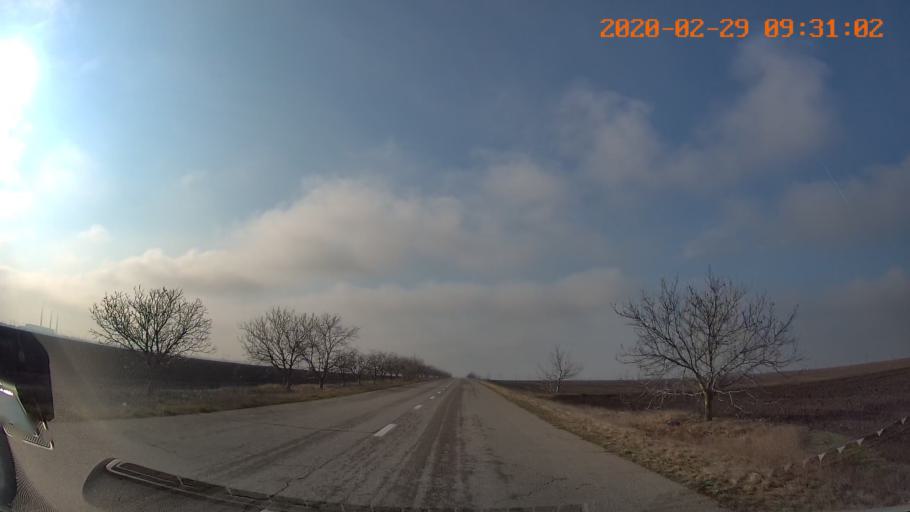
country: MD
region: Telenesti
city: Dnestrovsc
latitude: 46.6585
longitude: 29.9135
